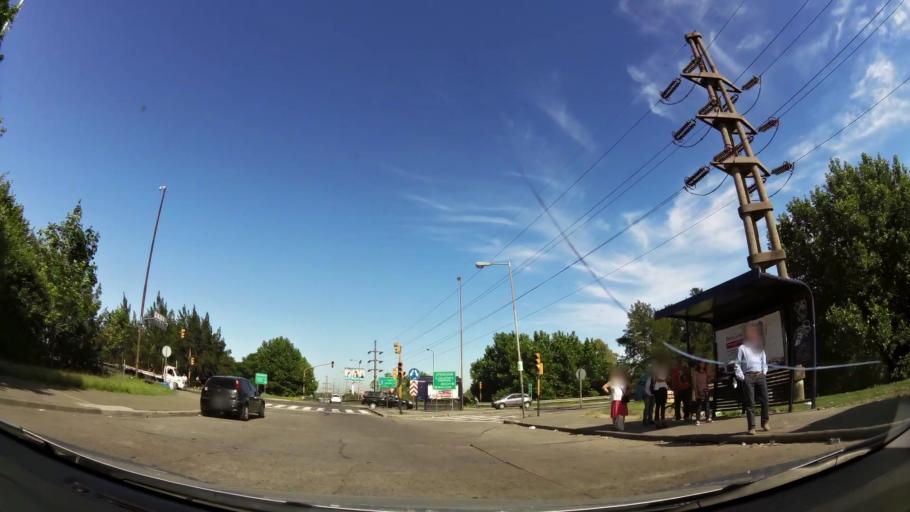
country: AR
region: Buenos Aires
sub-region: Partido de Tigre
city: Tigre
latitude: -34.4878
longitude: -58.5814
